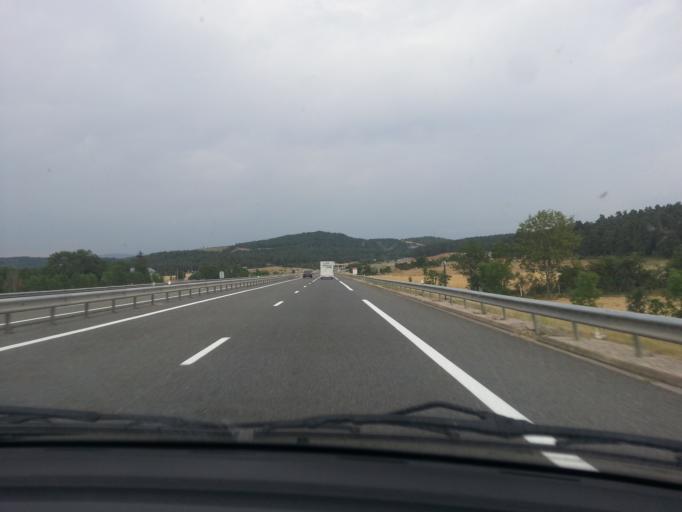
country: FR
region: Midi-Pyrenees
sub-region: Departement de l'Aveyron
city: Severac-le-Chateau
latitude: 44.3776
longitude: 3.1155
